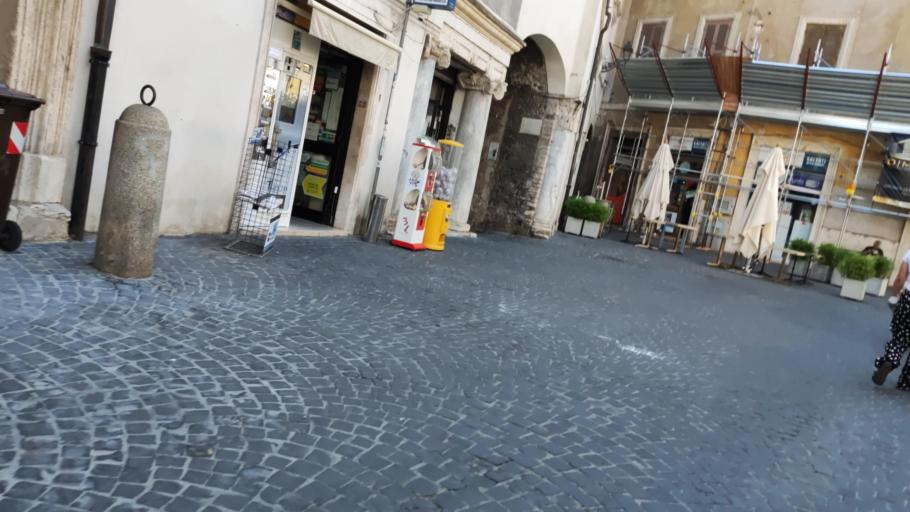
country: IT
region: Latium
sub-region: Citta metropolitana di Roma Capitale
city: Tivoli
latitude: 41.9644
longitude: 12.7993
